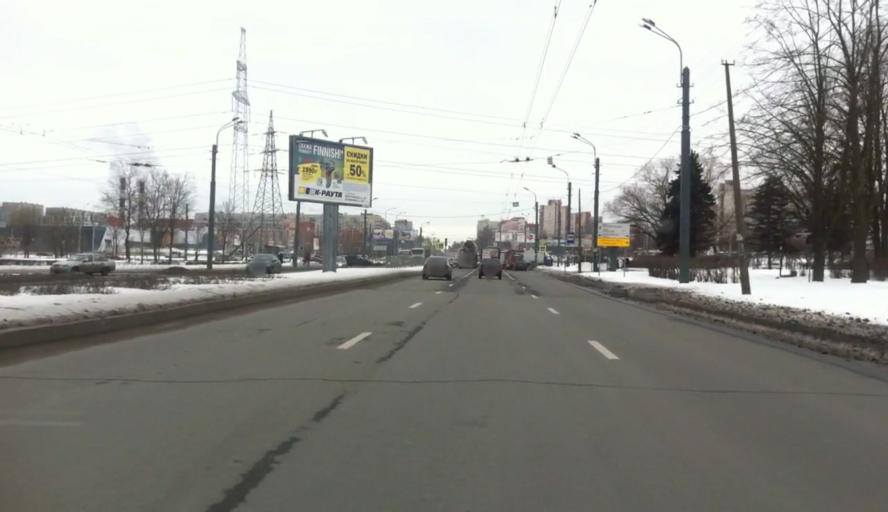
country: RU
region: St.-Petersburg
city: Uritsk
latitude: 59.8487
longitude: 30.1754
